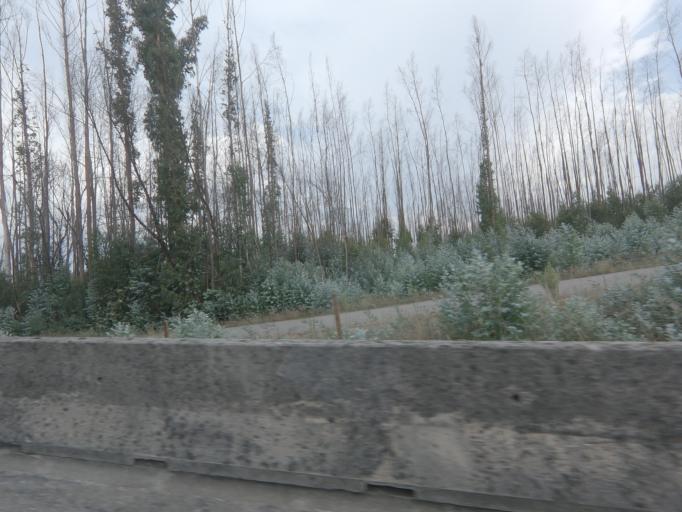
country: PT
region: Viseu
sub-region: Mortagua
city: Mortagua
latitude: 40.3468
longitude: -8.2088
